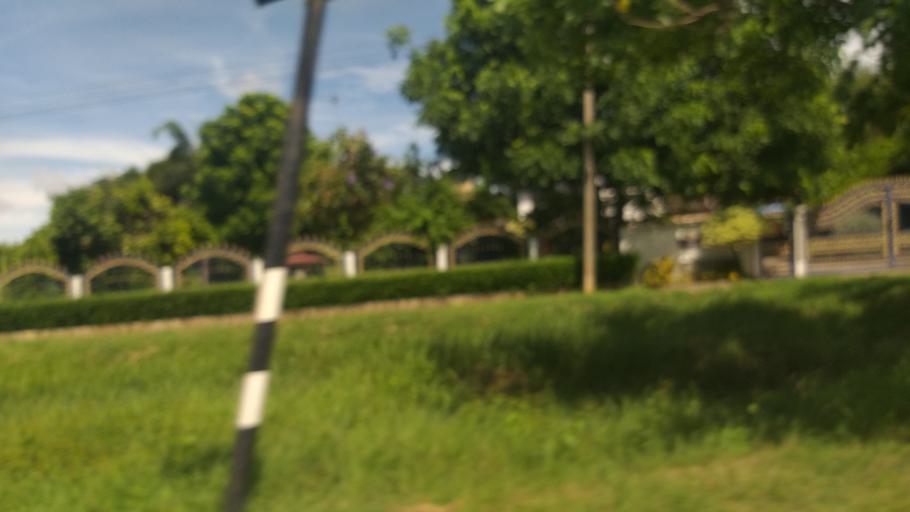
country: TH
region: Khon Kaen
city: Nong Ruea
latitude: 16.4663
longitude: 102.4419
